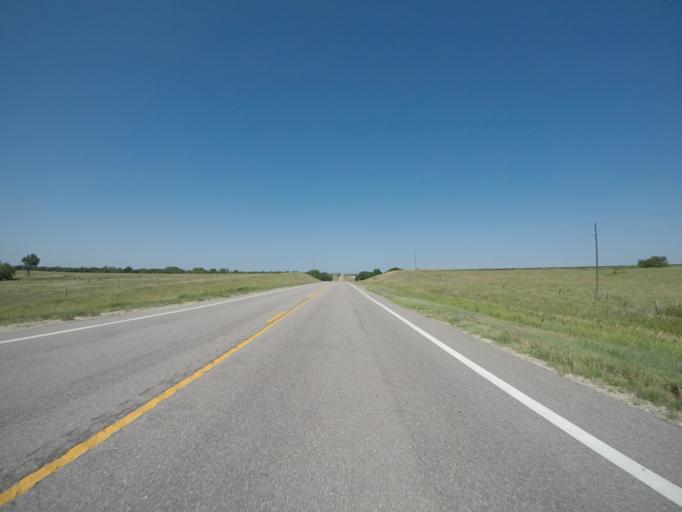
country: US
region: Kansas
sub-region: Cloud County
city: Concordia
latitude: 39.3648
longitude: -97.6437
